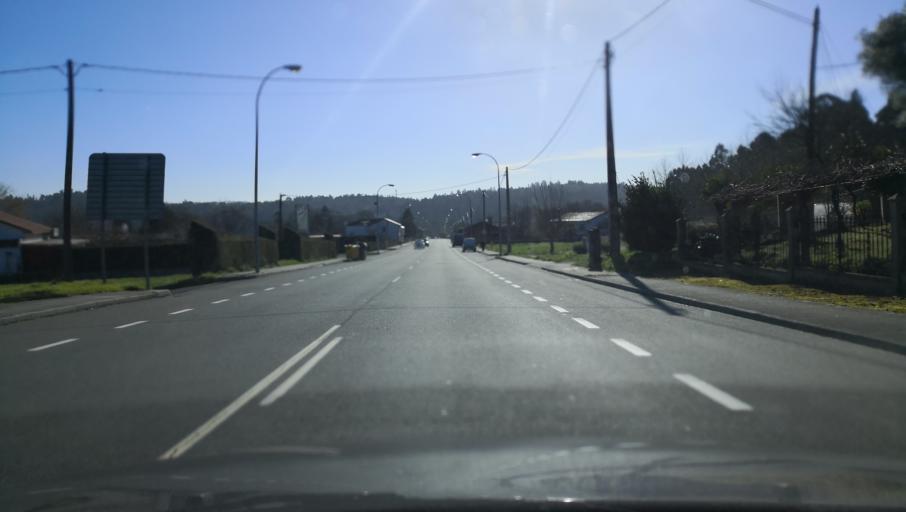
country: ES
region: Galicia
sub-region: Provincia de Pontevedra
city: Silleda
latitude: 42.7386
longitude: -8.3268
